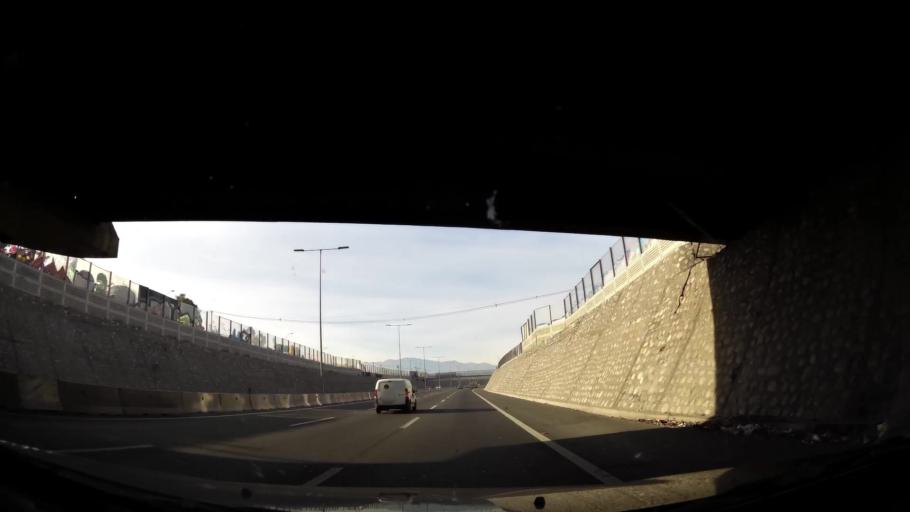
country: CL
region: Santiago Metropolitan
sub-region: Provincia de Santiago
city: La Pintana
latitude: -33.5898
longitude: -70.6087
